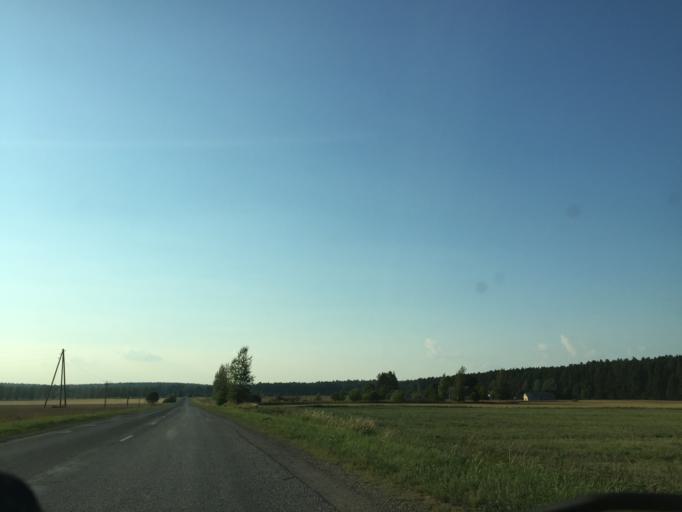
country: LV
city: Tervete
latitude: 56.4694
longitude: 23.4003
